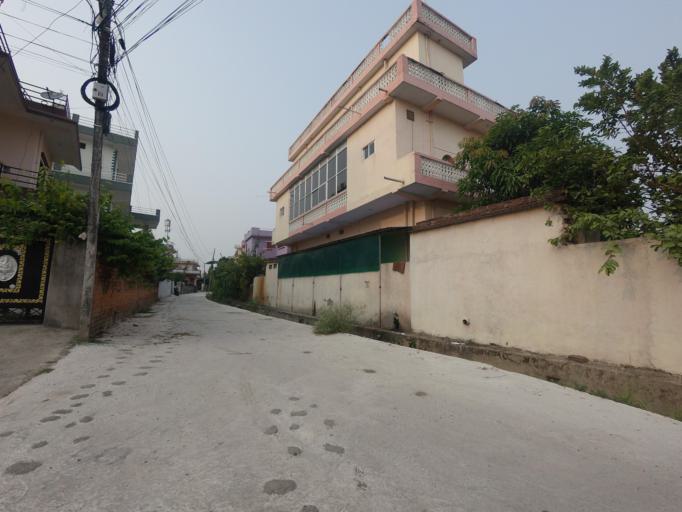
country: NP
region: Western Region
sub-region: Lumbini Zone
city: Bhairahawa
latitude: 27.5130
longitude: 83.4461
